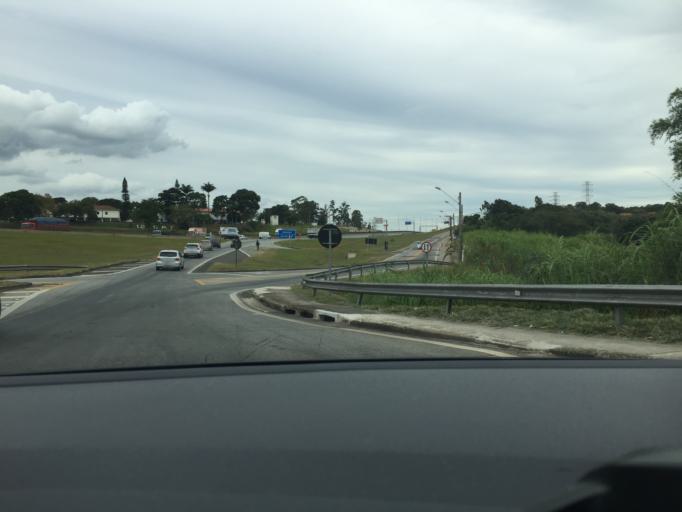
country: BR
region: Sao Paulo
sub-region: Jundiai
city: Jundiai
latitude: -23.2291
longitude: -46.8749
